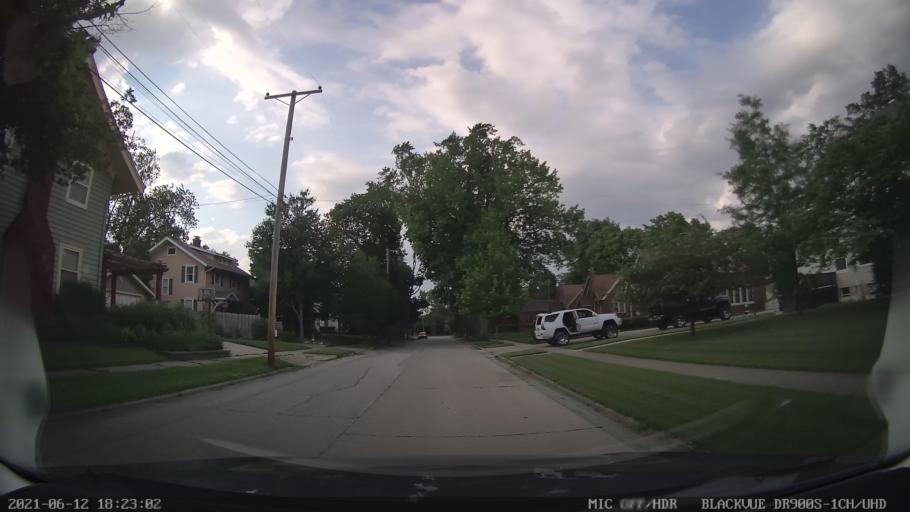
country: US
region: Illinois
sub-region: McLean County
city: Bloomington
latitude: 40.4784
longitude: -88.9719
